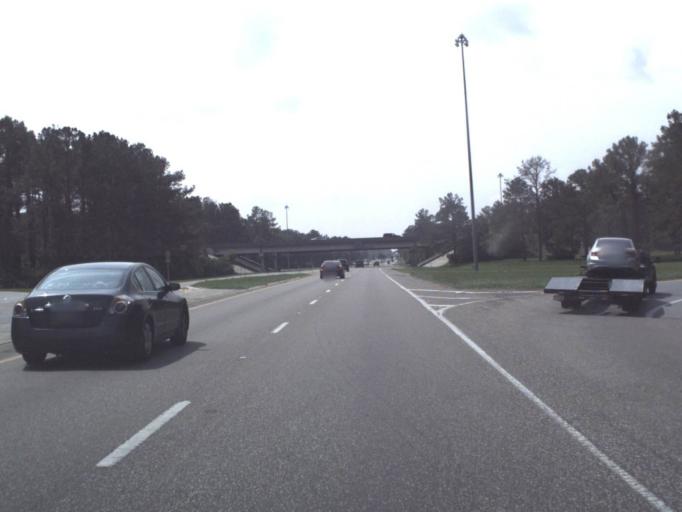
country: US
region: Florida
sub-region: Nassau County
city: Nassau Village-Ratliff
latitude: 30.4144
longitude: -81.7489
